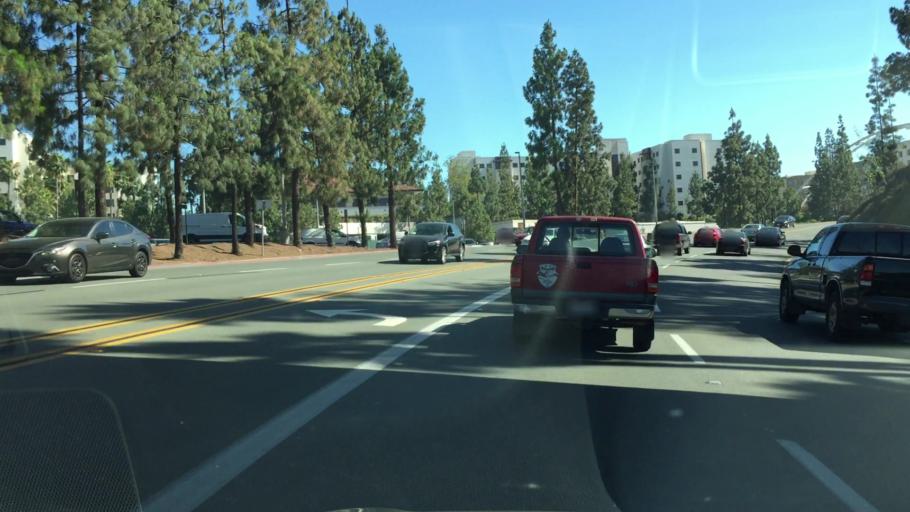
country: US
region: California
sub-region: San Diego County
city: La Mesa
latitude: 32.7745
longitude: -117.0679
